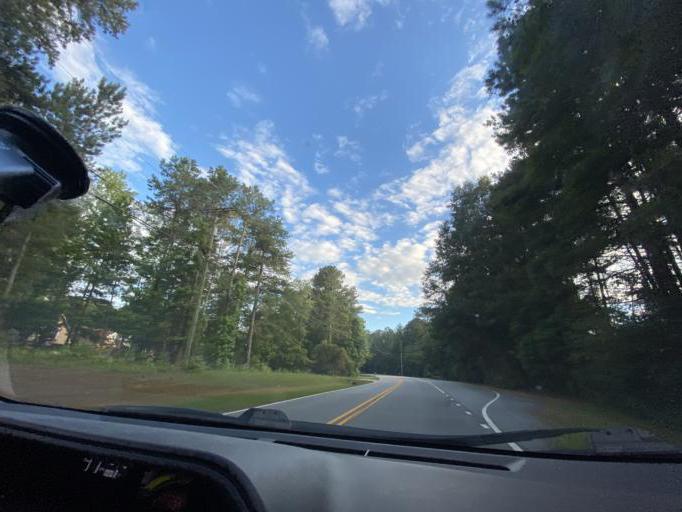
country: US
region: Georgia
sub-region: Fayette County
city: Peachtree City
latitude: 33.4234
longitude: -84.6511
